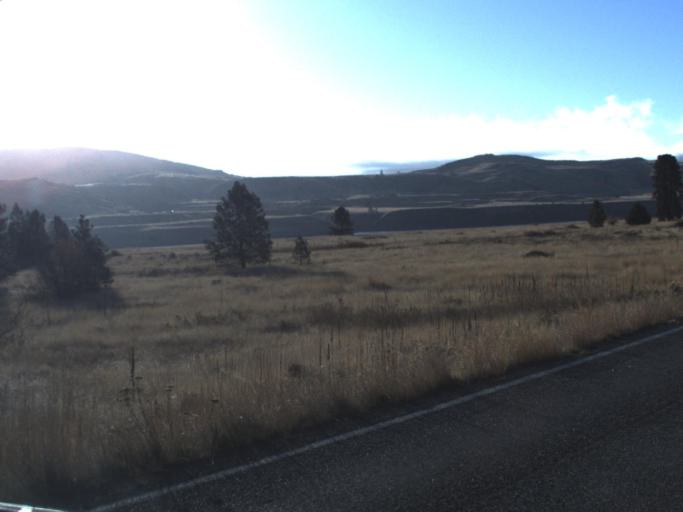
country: US
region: Washington
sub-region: Okanogan County
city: Coulee Dam
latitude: 47.9901
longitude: -118.6931
